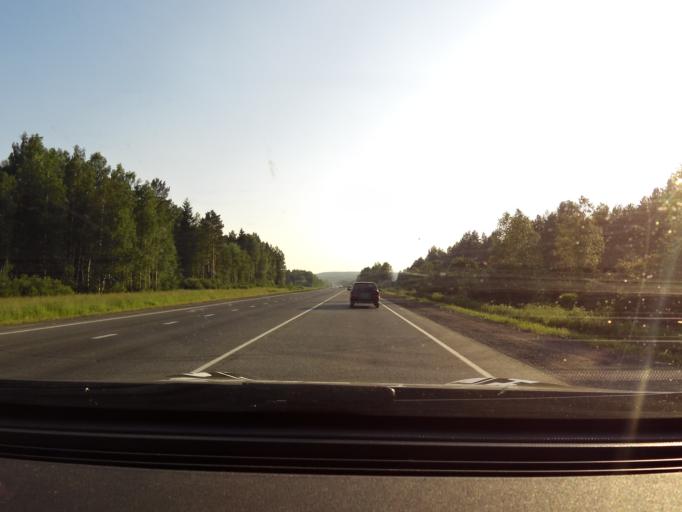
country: RU
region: Sverdlovsk
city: Atig
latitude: 56.7358
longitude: 59.4393
